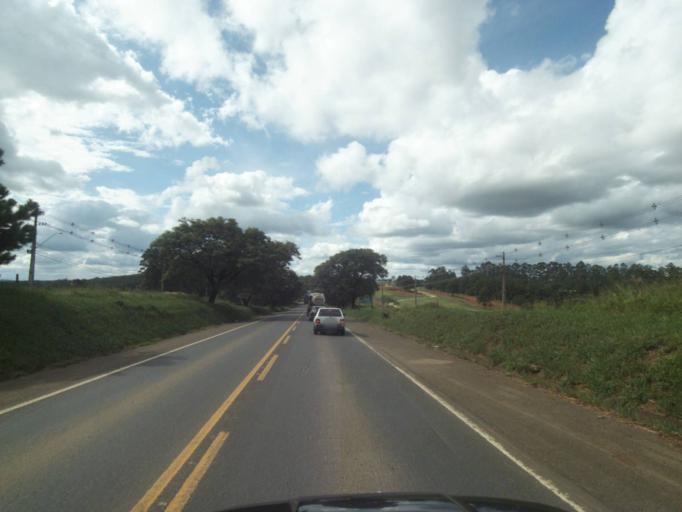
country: BR
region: Parana
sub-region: Telemaco Borba
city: Telemaco Borba
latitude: -24.3540
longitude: -50.6593
